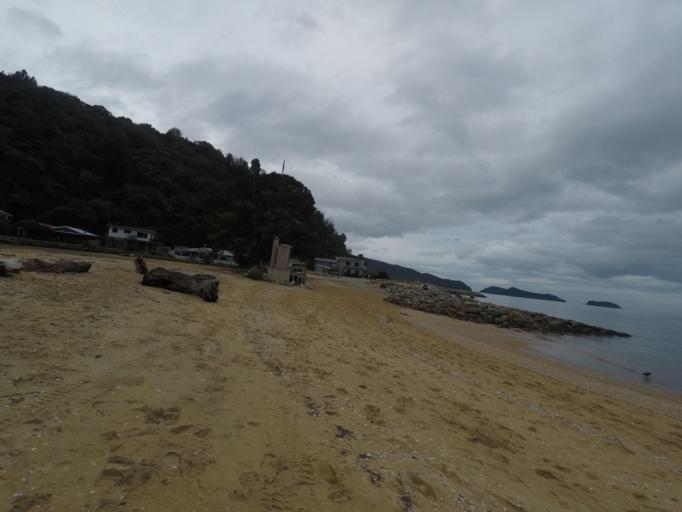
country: NZ
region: Tasman
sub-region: Tasman District
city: Motueka
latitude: -41.0097
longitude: 173.0075
